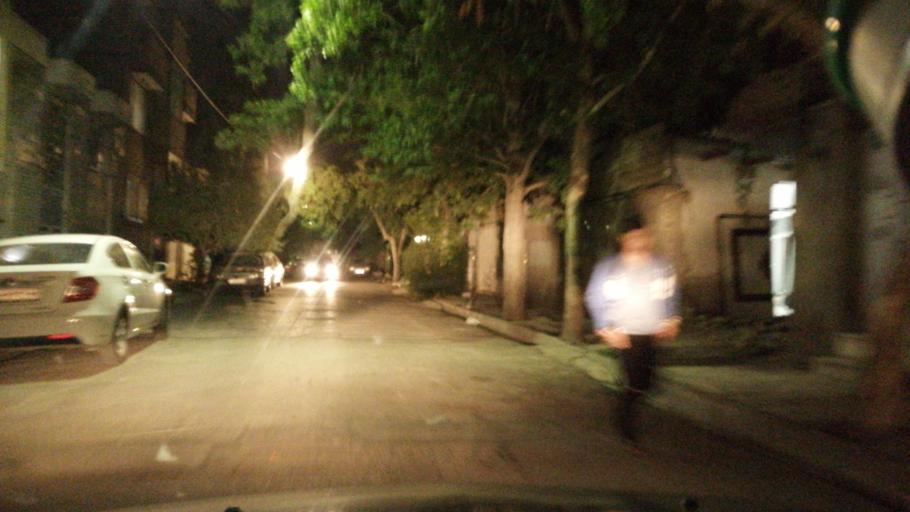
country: IR
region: Razavi Khorasan
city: Mashhad
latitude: 36.3080
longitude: 59.6031
